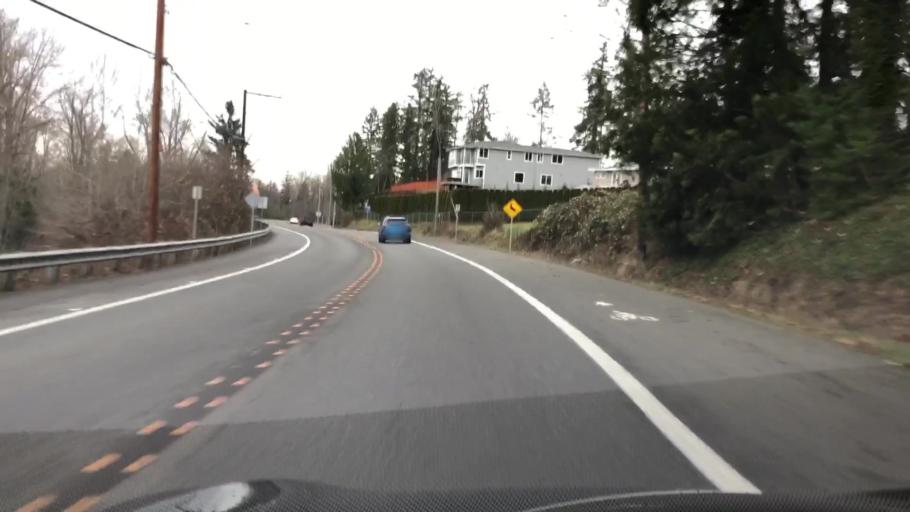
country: US
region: Washington
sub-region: King County
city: Sammamish
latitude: 47.6549
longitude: -122.0917
